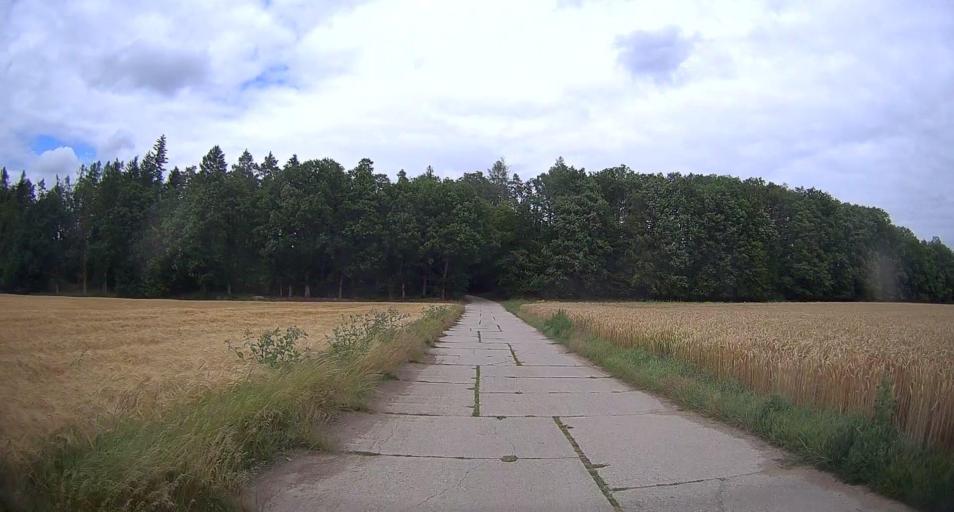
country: CZ
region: South Moravian
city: Lipuvka
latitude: 49.3346
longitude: 16.5382
